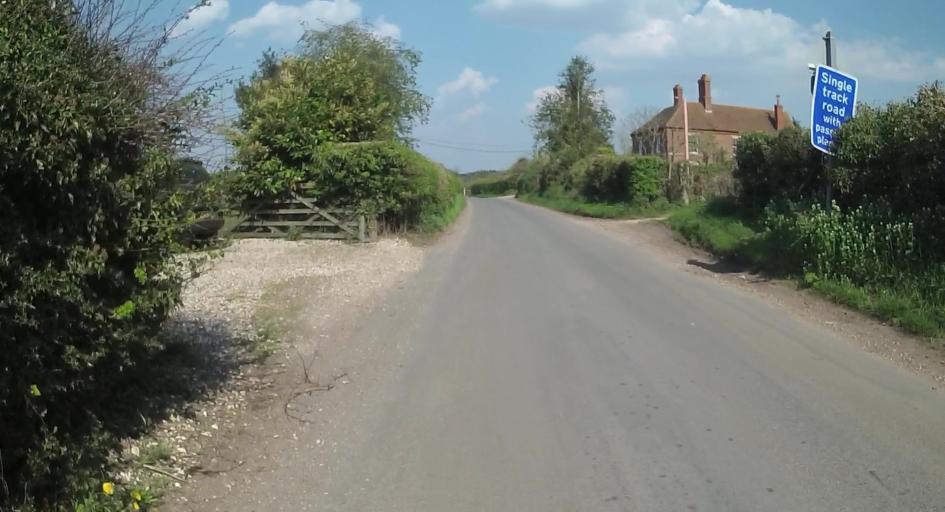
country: GB
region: England
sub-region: Hampshire
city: Tadley
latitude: 51.3933
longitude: -1.1121
